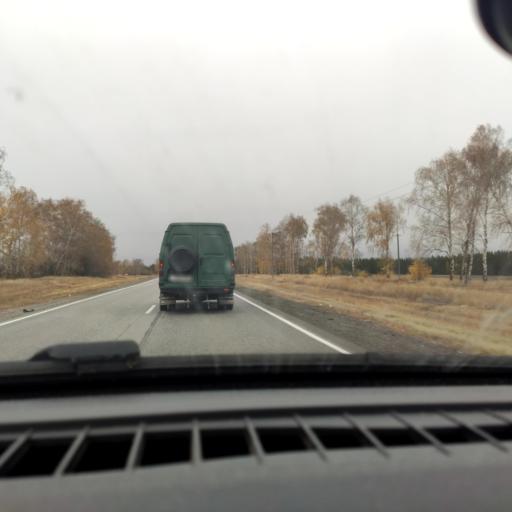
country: RU
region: Voronezj
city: Uryv-Pokrovka
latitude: 51.0630
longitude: 38.9937
